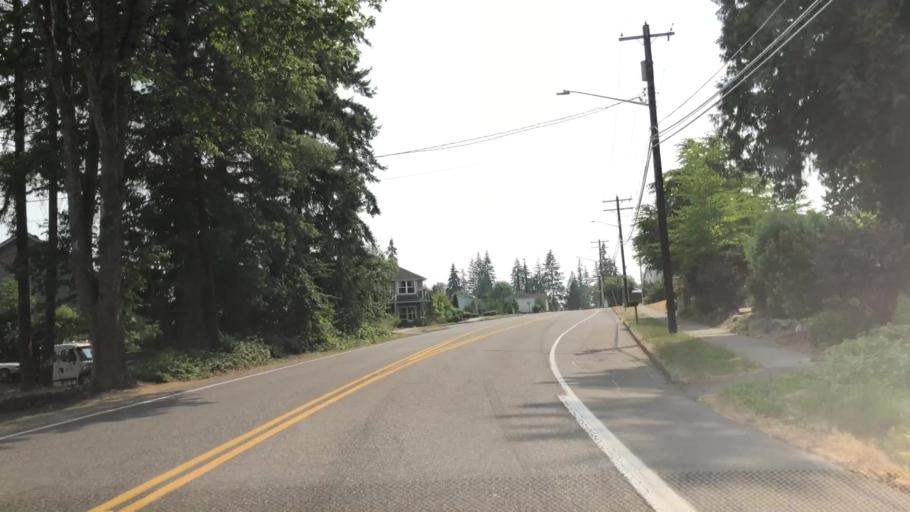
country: US
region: Washington
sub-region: Snohomish County
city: Martha Lake
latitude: 47.8169
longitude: -122.2433
